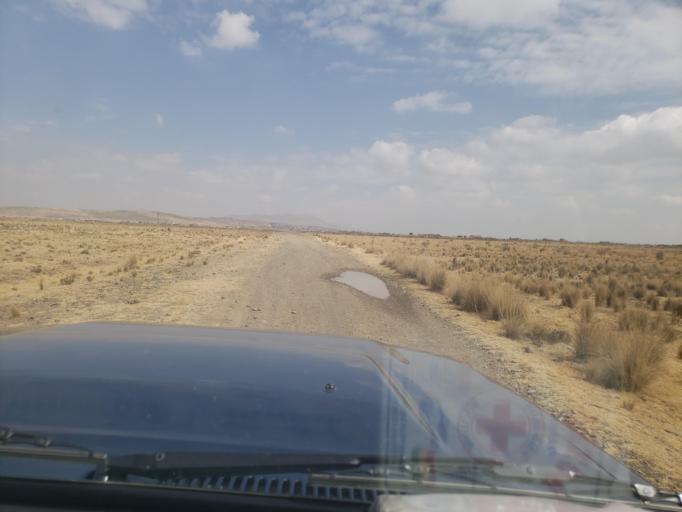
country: BO
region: La Paz
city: Batallas
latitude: -16.4094
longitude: -68.4440
